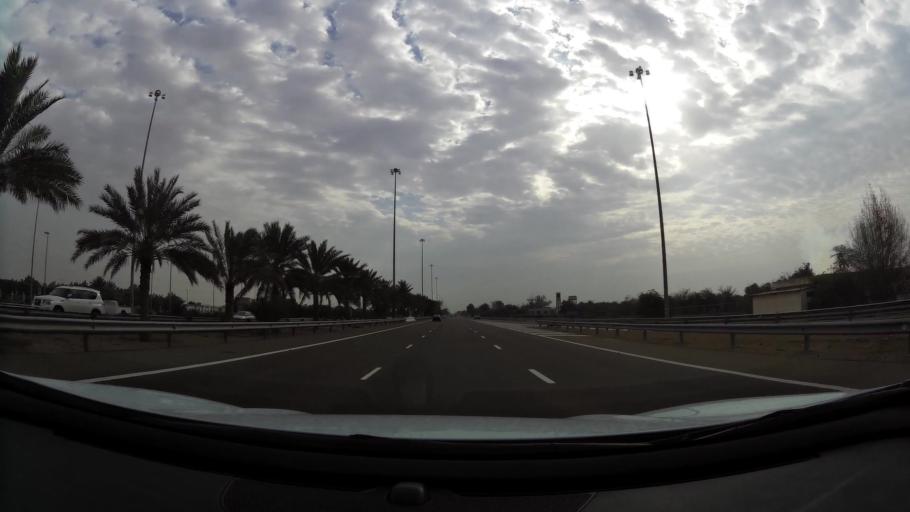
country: AE
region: Abu Dhabi
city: Al Ain
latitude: 24.2040
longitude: 55.3907
